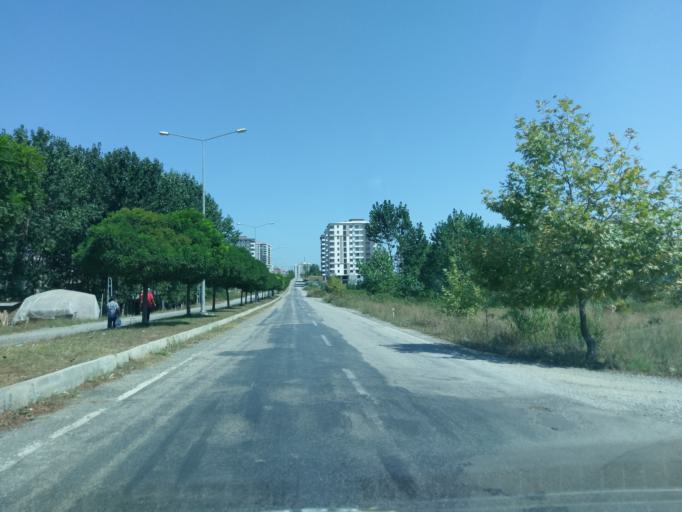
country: TR
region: Samsun
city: Samsun
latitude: 41.2585
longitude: 36.3098
